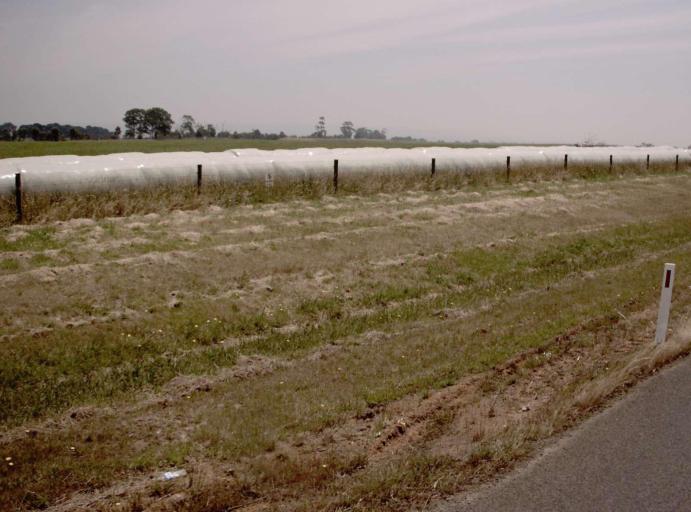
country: AU
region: Victoria
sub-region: Latrobe
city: Traralgon
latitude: -38.2502
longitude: 146.6198
